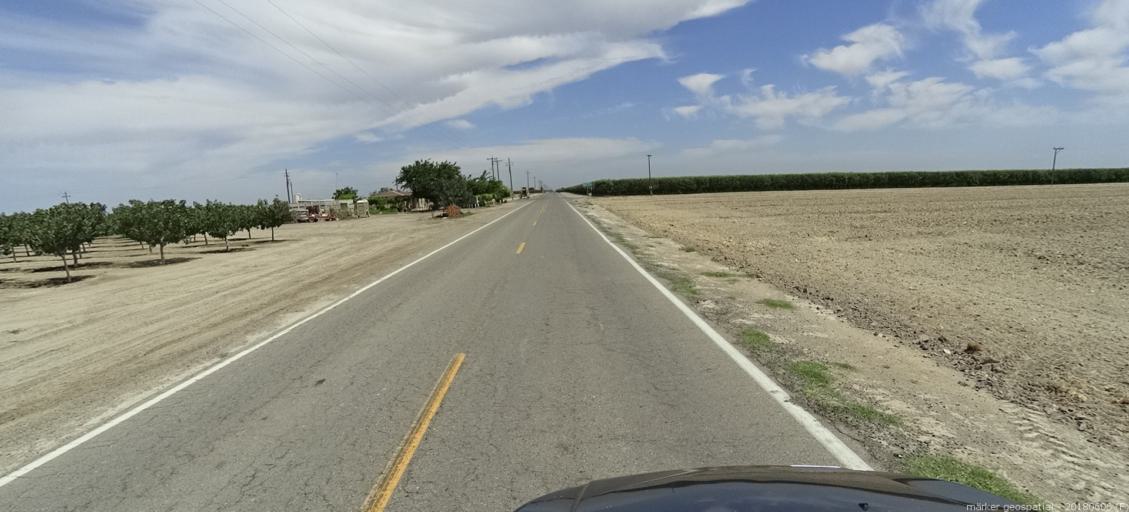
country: US
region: California
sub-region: Fresno County
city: Firebaugh
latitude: 36.9511
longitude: -120.3826
